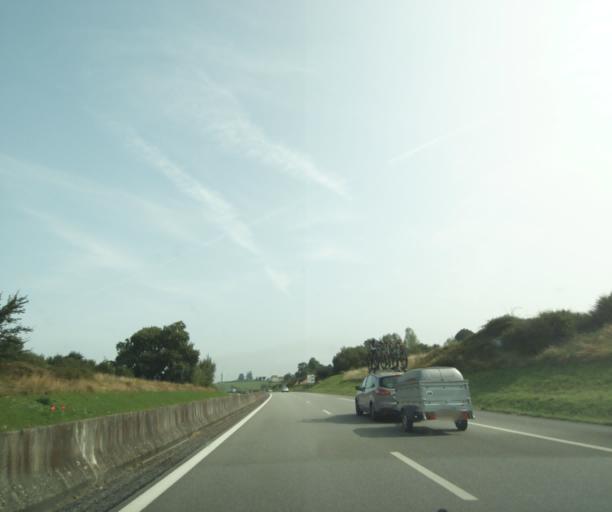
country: FR
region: Lower Normandy
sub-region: Departement de l'Orne
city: Radon
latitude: 48.5277
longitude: 0.1581
